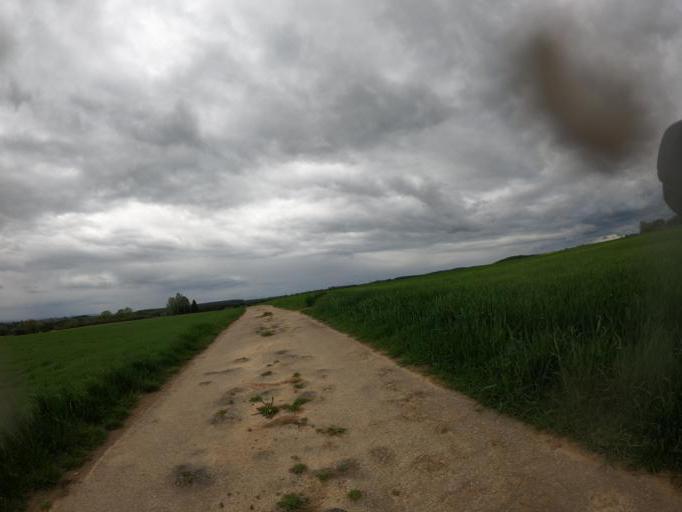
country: DE
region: Baden-Wuerttemberg
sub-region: Karlsruhe Region
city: Nagold
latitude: 48.5271
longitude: 8.7008
